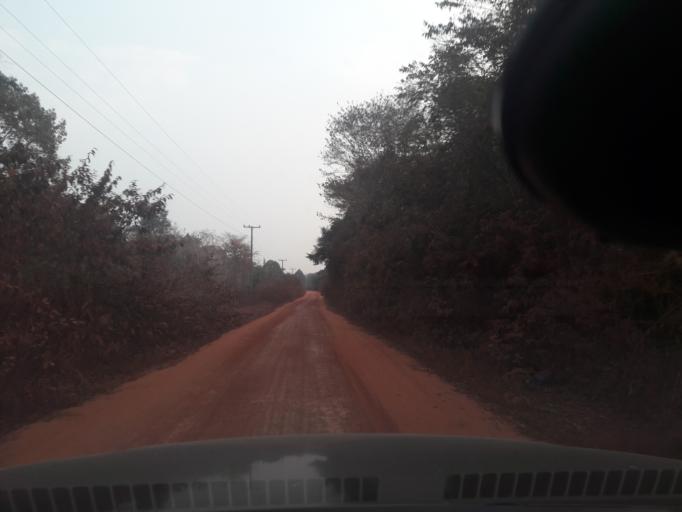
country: TH
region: Nong Khai
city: Si Chiang Mai
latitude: 18.0510
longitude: 102.4880
